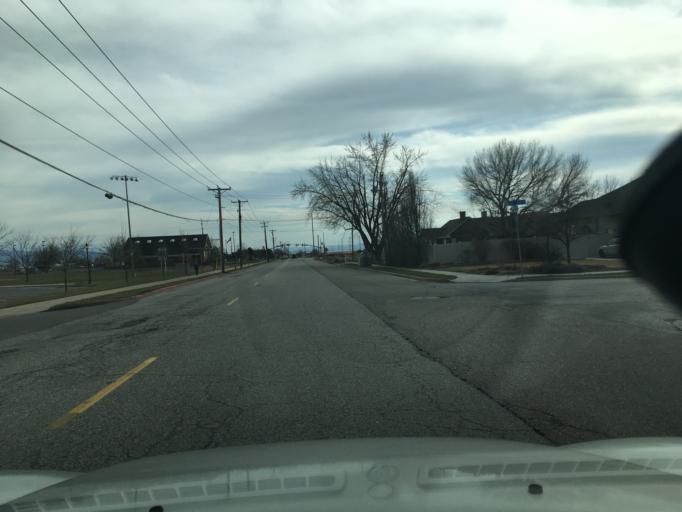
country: US
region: Utah
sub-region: Davis County
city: Layton
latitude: 41.0703
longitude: -112.0070
